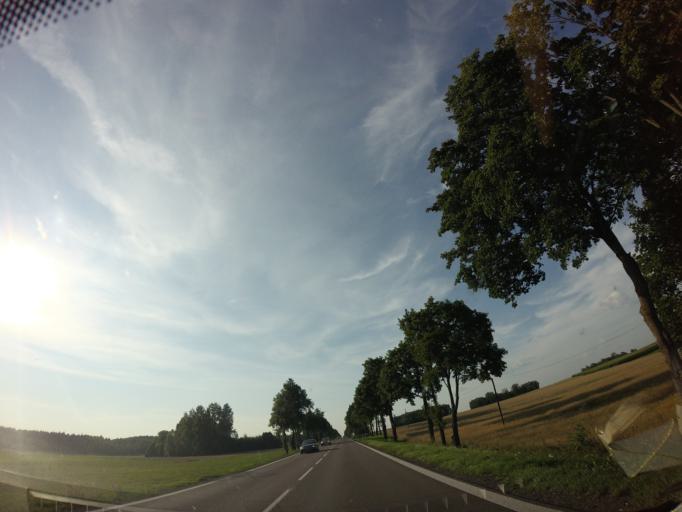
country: PL
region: Podlasie
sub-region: Powiat sokolski
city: Janow
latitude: 53.4197
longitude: 23.1123
